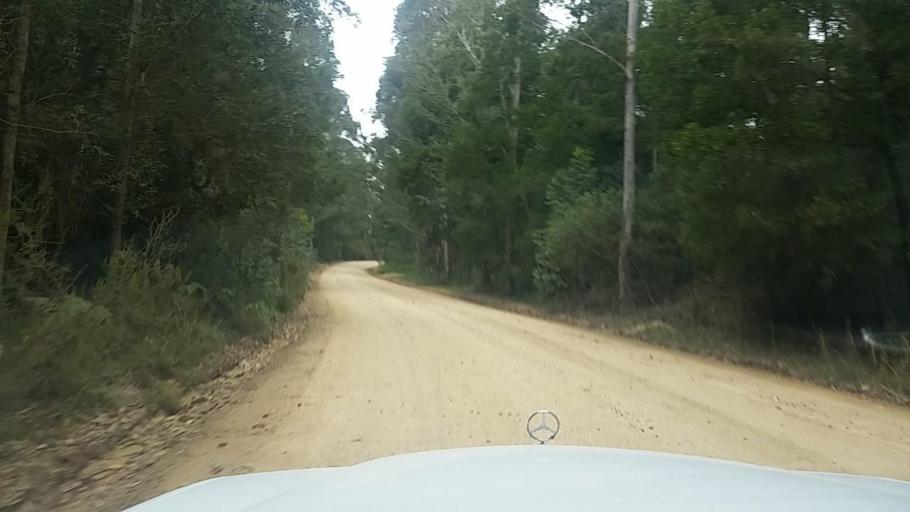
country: ZA
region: Western Cape
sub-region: Eden District Municipality
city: Knysna
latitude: -33.9852
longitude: 23.1459
